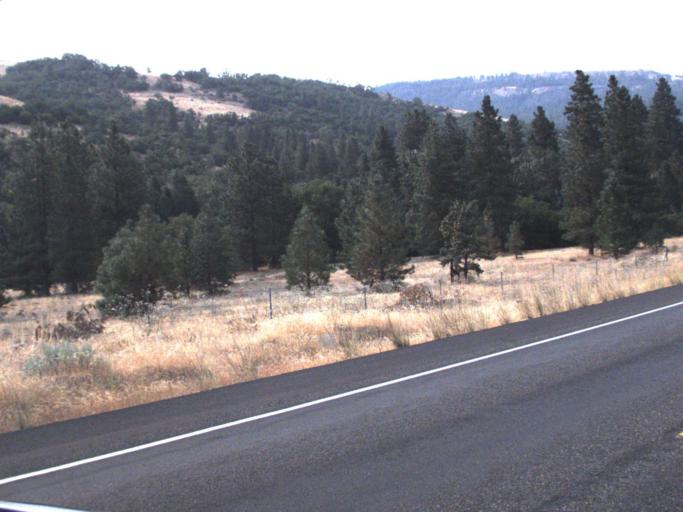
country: US
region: Washington
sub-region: Klickitat County
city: Goldendale
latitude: 46.0558
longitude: -120.5666
